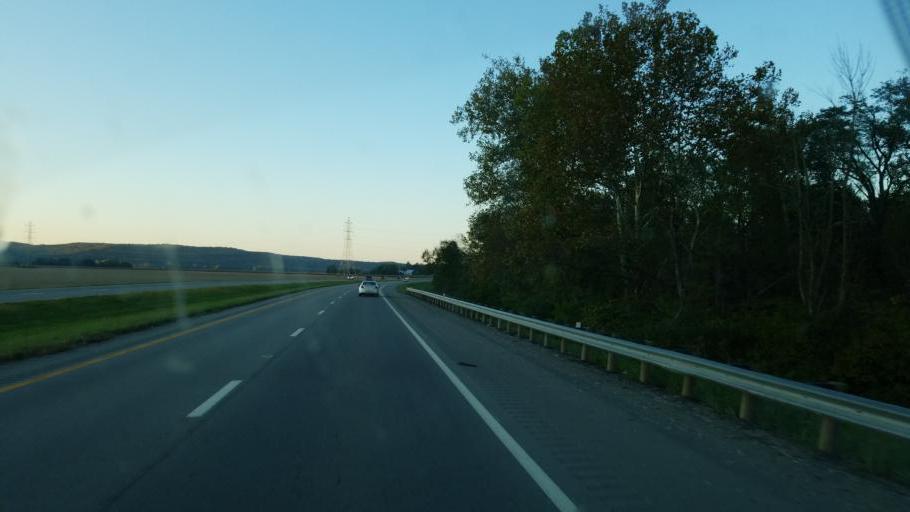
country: US
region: Ohio
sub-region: Pike County
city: Piketon
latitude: 39.0329
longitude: -83.0273
